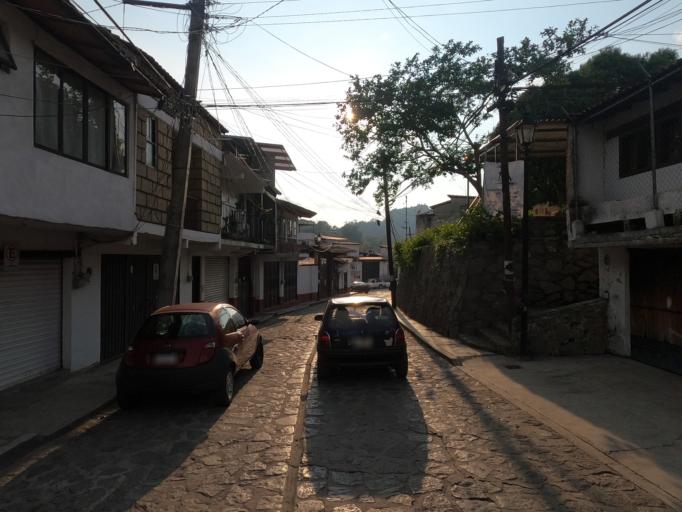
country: MX
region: Mexico
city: Valle de Bravo
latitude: 19.1992
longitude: -100.1314
